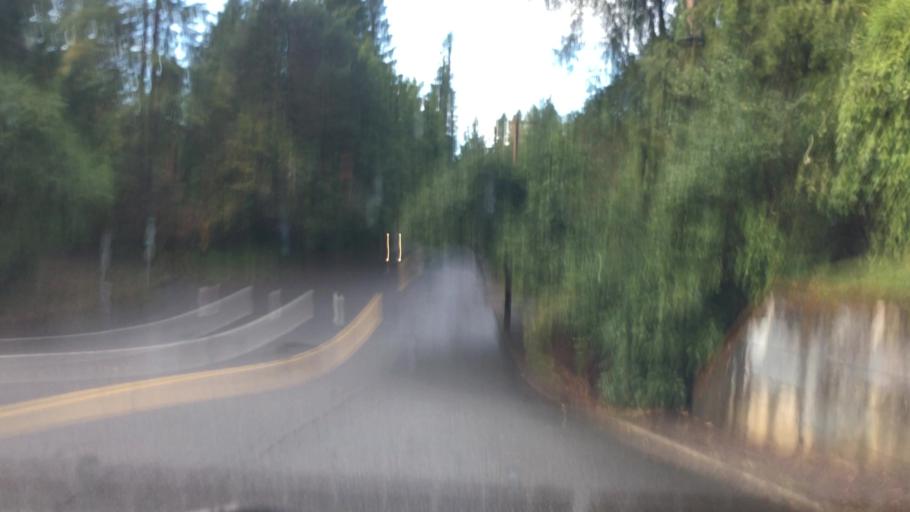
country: US
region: Oregon
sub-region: Multnomah County
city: Portland
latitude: 45.4818
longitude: -122.7077
